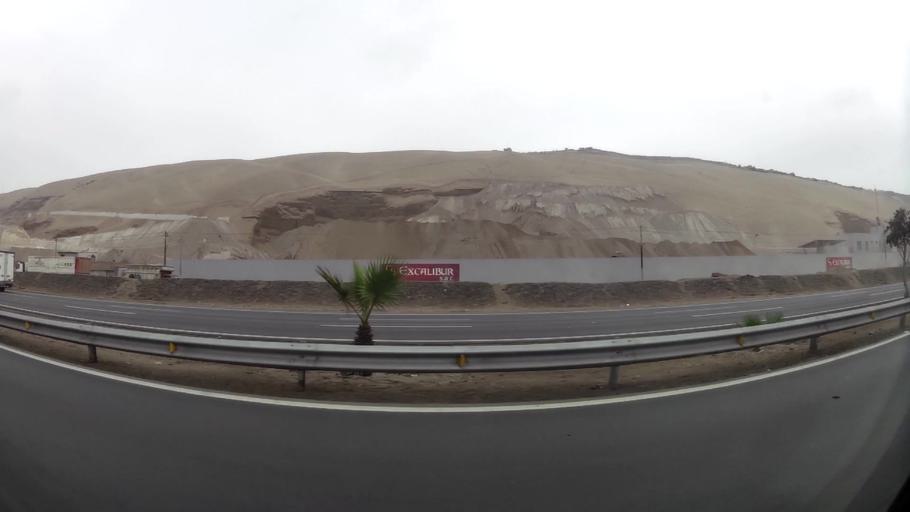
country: PE
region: Lima
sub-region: Lima
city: Surco
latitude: -12.2408
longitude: -76.9471
